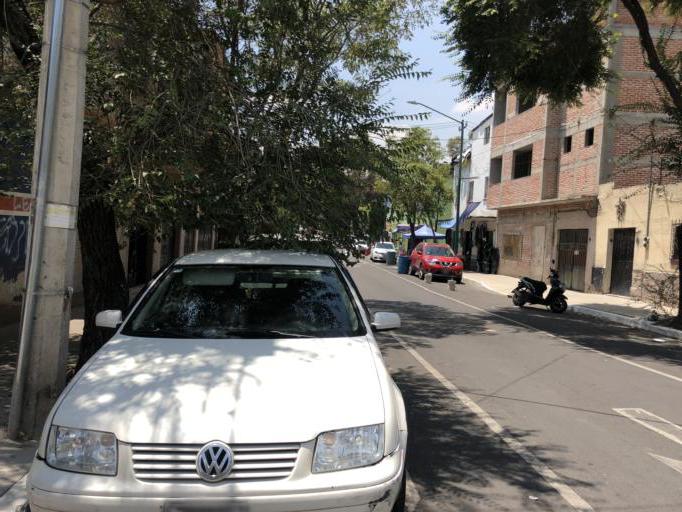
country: MX
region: Mexico City
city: Cuauhtemoc
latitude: 19.4557
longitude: -99.1333
